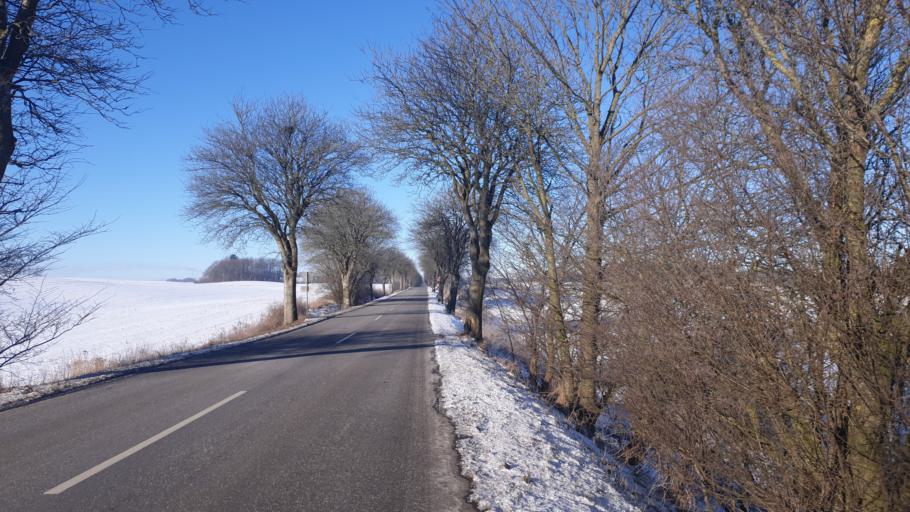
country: DK
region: Central Jutland
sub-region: Hedensted Kommune
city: Hedensted
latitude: 55.7970
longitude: 9.7434
